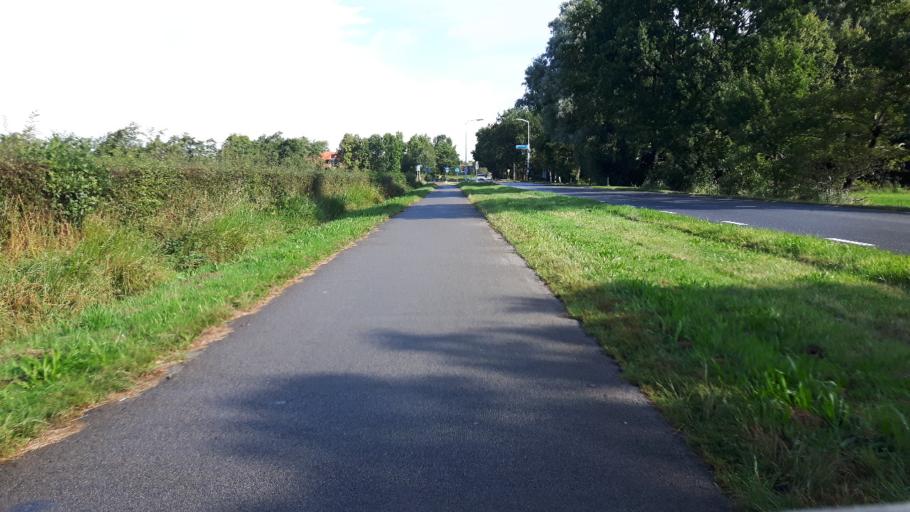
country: NL
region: Friesland
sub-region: Gemeente Smallingerland
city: Drachten
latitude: 53.0764
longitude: 6.0981
